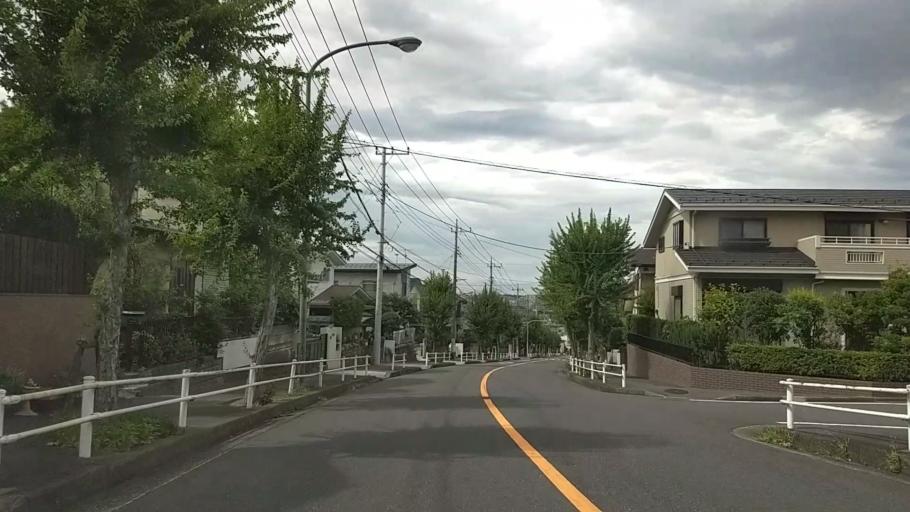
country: JP
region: Tokyo
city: Hachioji
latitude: 35.6384
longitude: 139.3457
